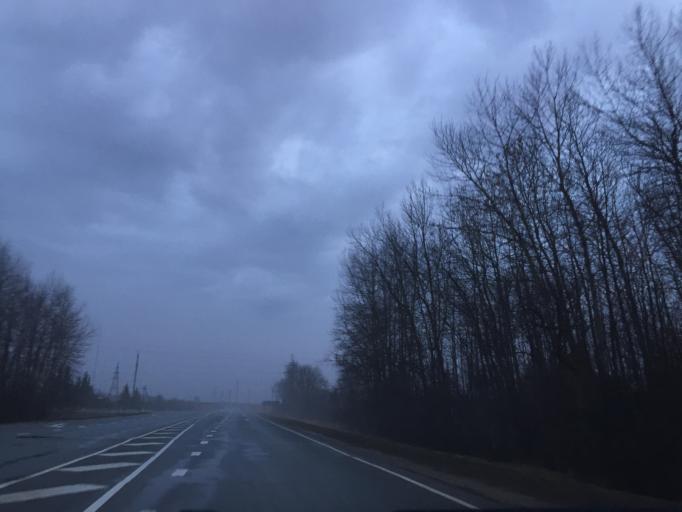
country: EE
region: Laeaene
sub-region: Lihula vald
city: Lihula
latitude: 58.6816
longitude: 23.8131
